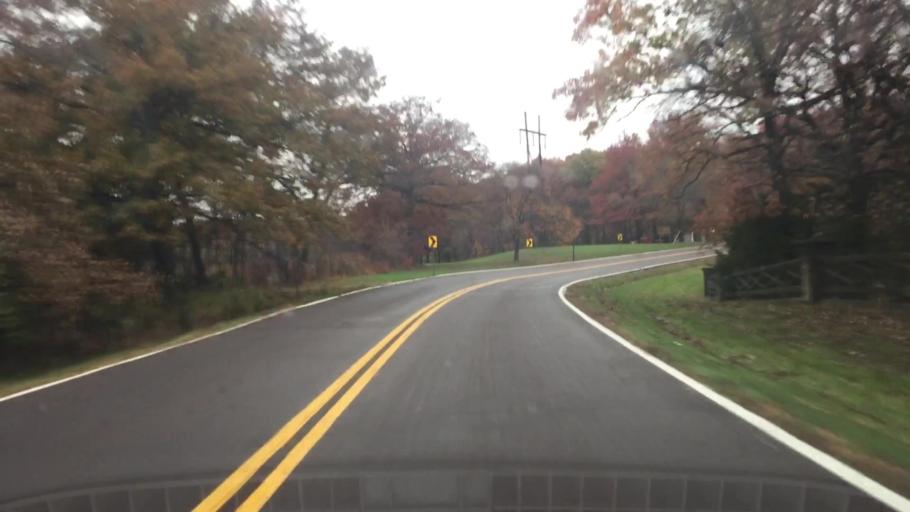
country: US
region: Missouri
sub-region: Boone County
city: Columbia
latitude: 38.8644
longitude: -92.3168
